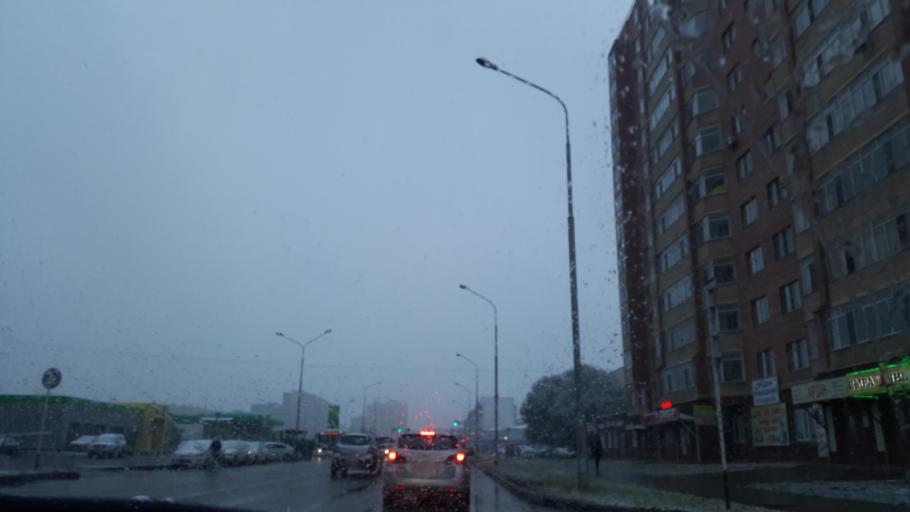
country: KZ
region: Astana Qalasy
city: Astana
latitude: 51.1573
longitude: 71.4967
